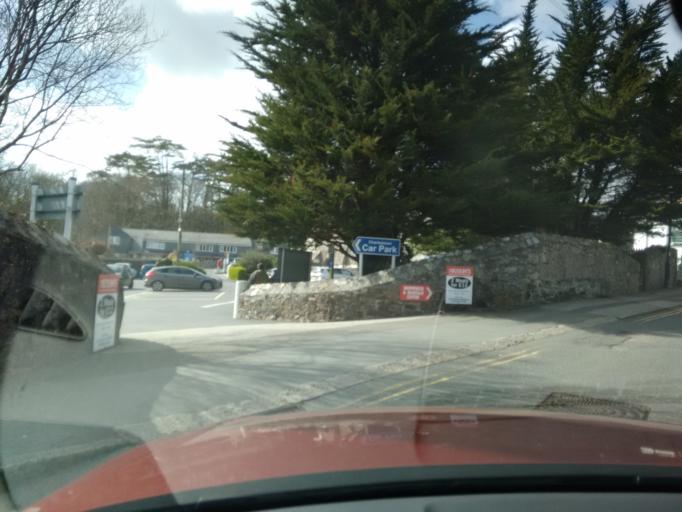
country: GB
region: England
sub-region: Cornwall
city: St Austell
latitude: 50.3324
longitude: -4.7579
